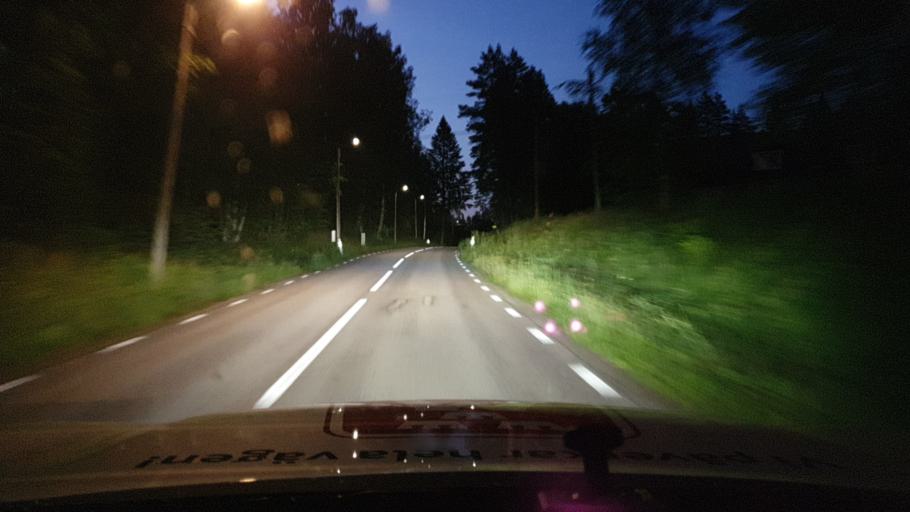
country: SE
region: OErebro
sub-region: Karlskoga Kommun
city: Karlskoga
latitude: 59.4002
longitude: 14.6386
